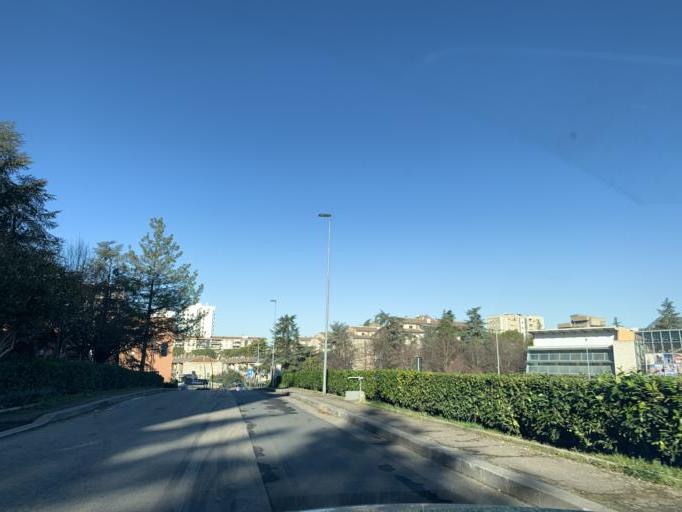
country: IT
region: Umbria
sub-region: Provincia di Terni
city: Terni
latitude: 42.5498
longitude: 12.6339
